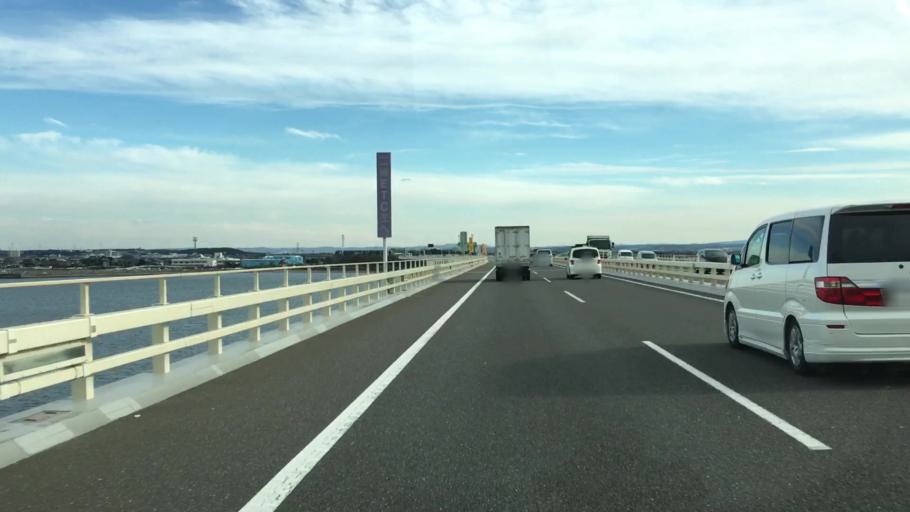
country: JP
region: Chiba
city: Kisarazu
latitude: 35.4408
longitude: 139.9091
